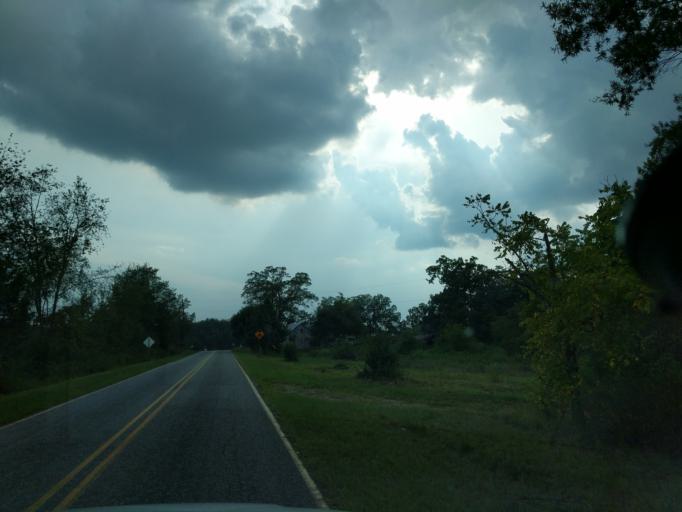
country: US
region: North Carolina
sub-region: Rutherford County
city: Spindale
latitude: 35.2117
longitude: -81.9879
